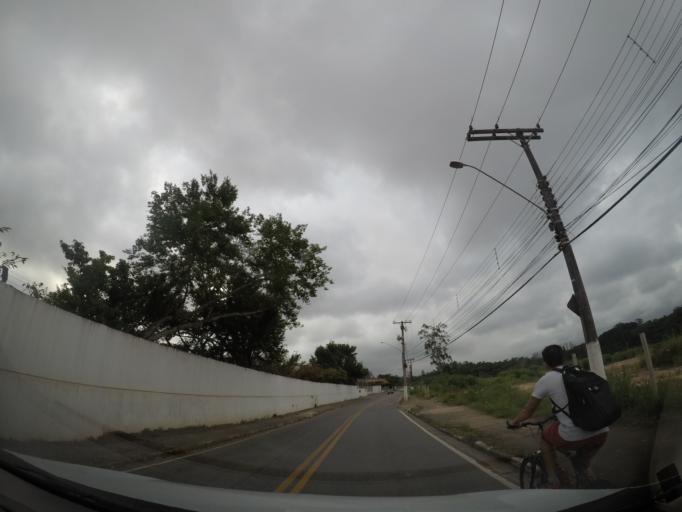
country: BR
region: Sao Paulo
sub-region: Aruja
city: Aruja
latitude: -23.4003
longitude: -46.3374
